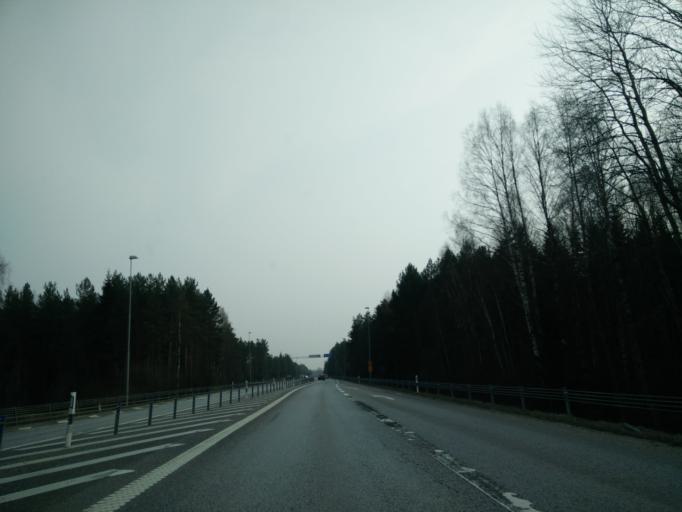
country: SE
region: Vaermland
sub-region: Forshaga Kommun
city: Forshaga
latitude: 59.4573
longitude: 13.4166
